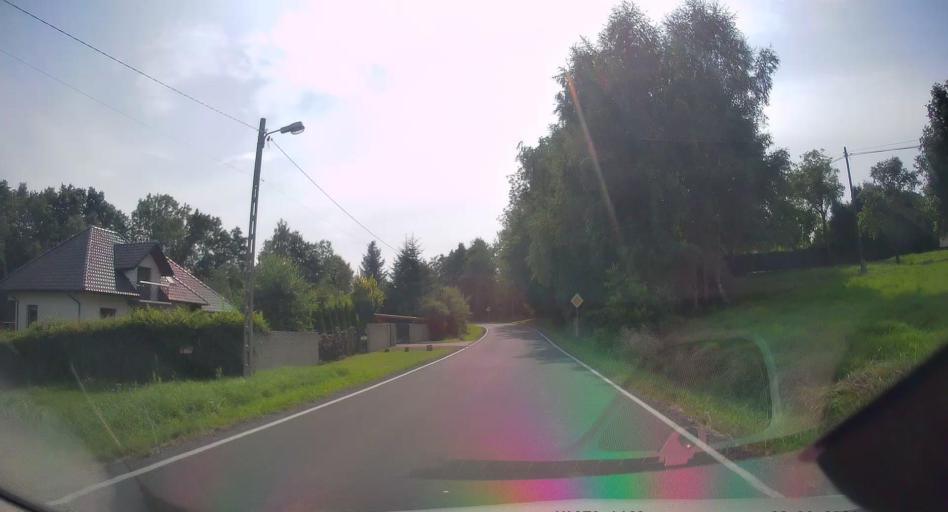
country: PL
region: Lesser Poland Voivodeship
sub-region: Powiat wielicki
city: Pawlikowice
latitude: 49.9477
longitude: 20.0396
